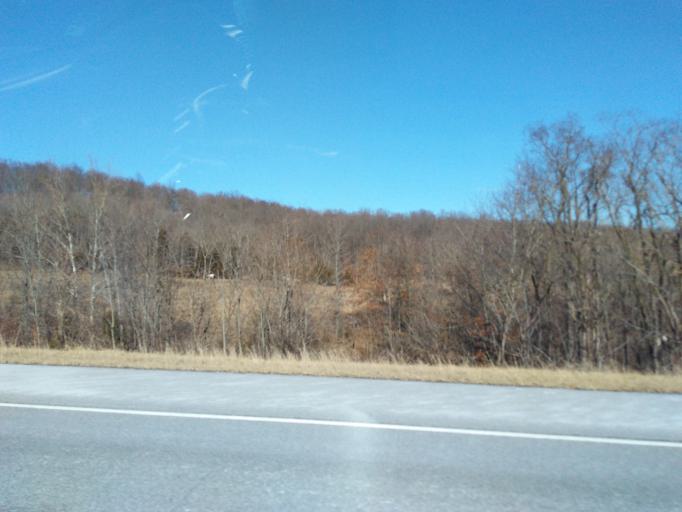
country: US
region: Illinois
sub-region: Johnson County
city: Vienna
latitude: 37.3373
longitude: -88.7831
